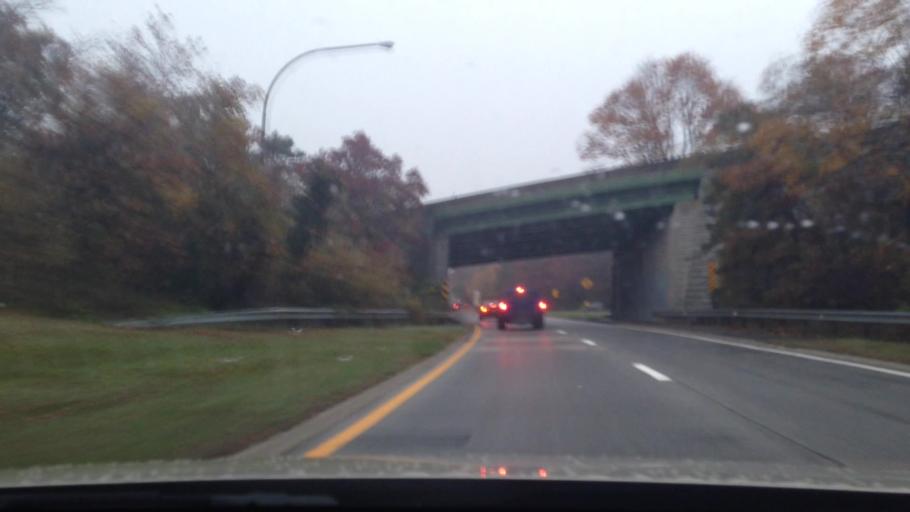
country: US
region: New York
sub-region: Suffolk County
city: Bay Wood
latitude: 40.7466
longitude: -73.2789
